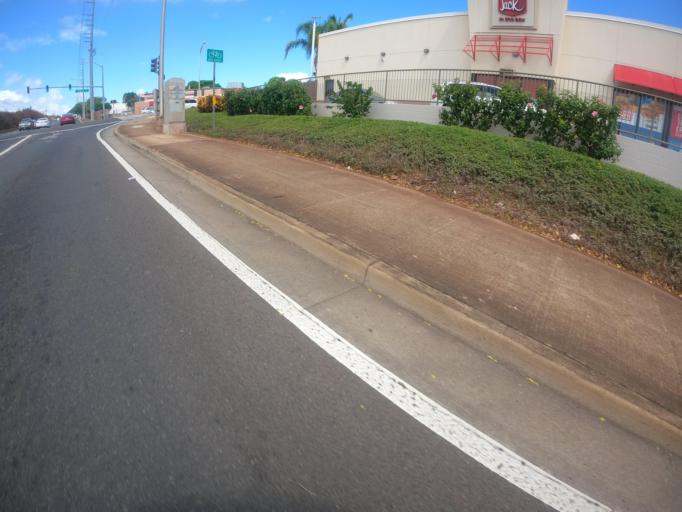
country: US
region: Hawaii
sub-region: Honolulu County
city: Royal Kunia
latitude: 21.3879
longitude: -158.0342
